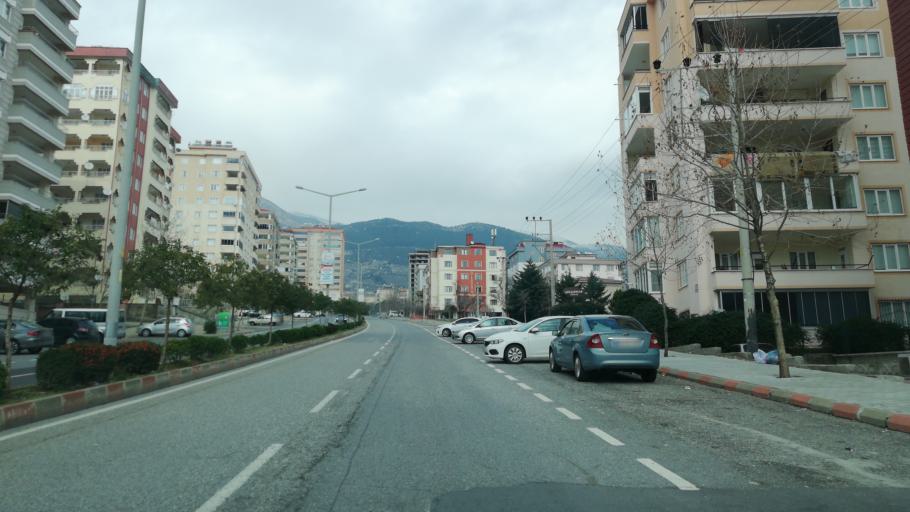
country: TR
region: Kahramanmaras
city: Kahramanmaras
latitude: 37.5892
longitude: 36.8629
